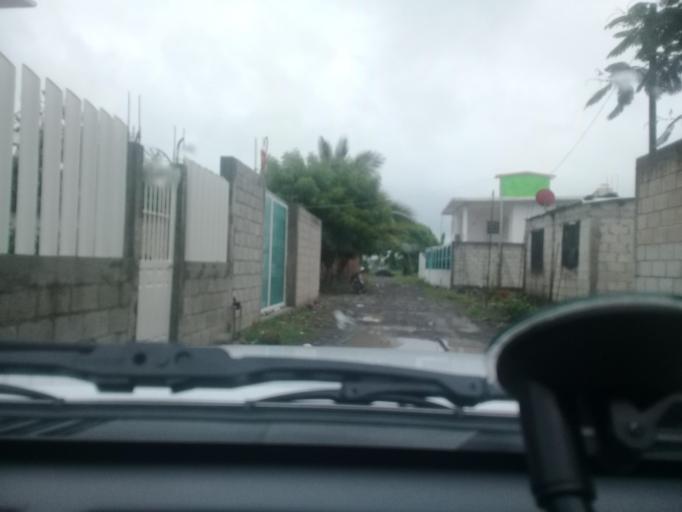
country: MX
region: Veracruz
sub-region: La Antigua
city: Nicolas Blanco (San Pancho)
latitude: 19.3393
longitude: -96.3612
